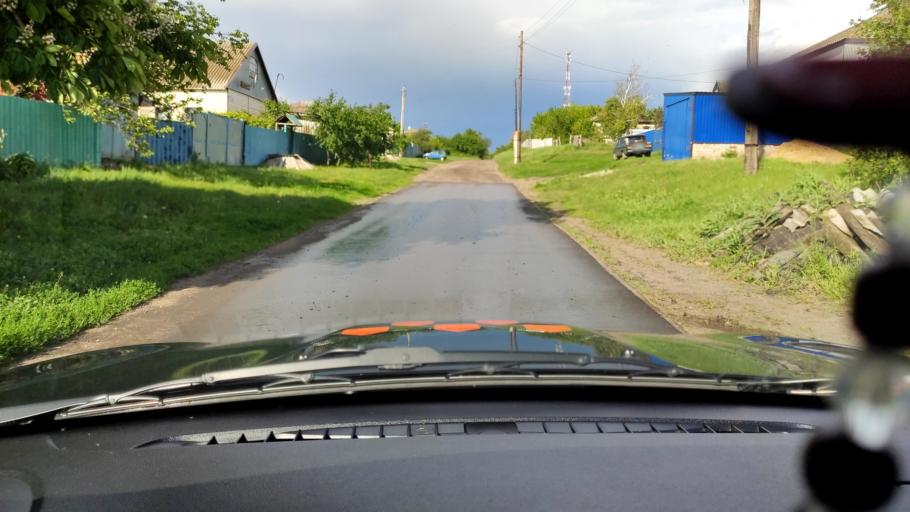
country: RU
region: Voronezj
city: Uryv-Pokrovka
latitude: 51.1098
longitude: 39.1708
